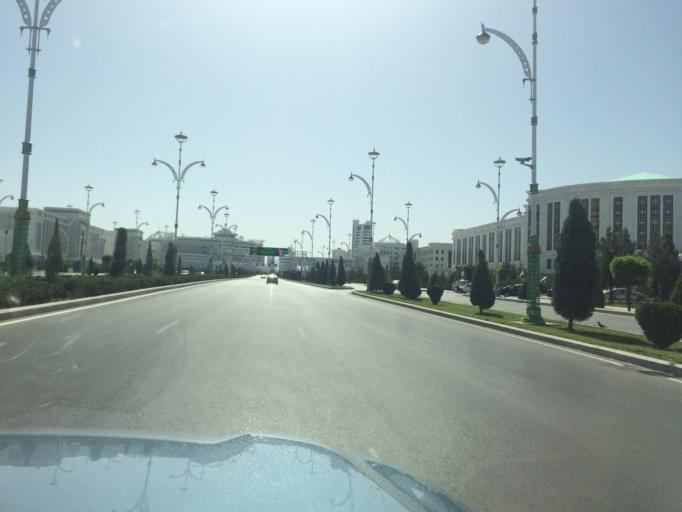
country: TM
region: Ahal
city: Ashgabat
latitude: 37.8983
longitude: 58.3620
